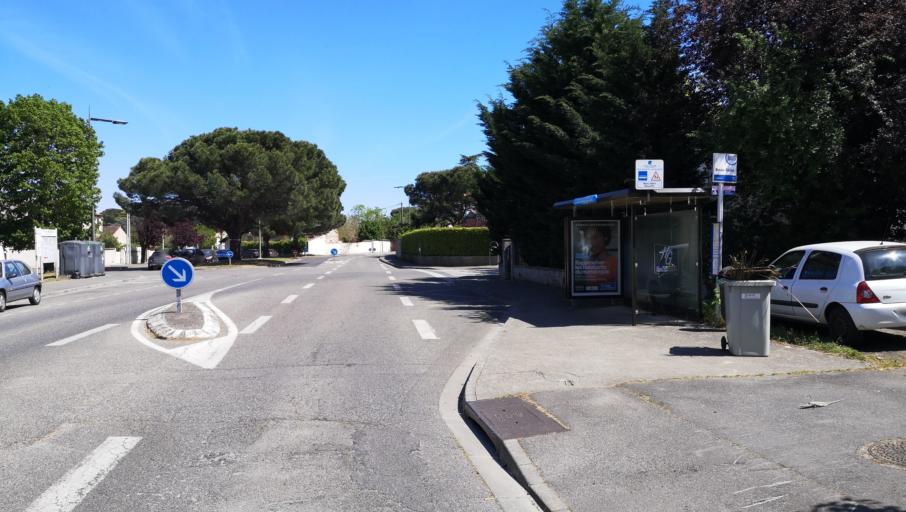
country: FR
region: Midi-Pyrenees
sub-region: Departement de la Haute-Garonne
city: Beauzelle
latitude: 43.6702
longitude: 1.3737
